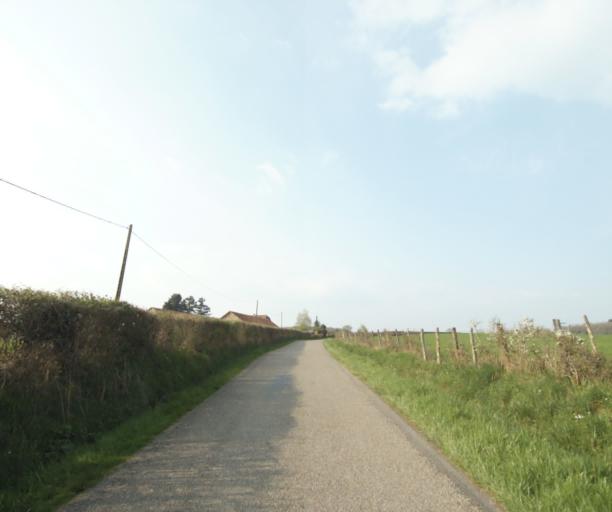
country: FR
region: Bourgogne
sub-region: Departement de Saone-et-Loire
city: Matour
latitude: 46.4707
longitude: 4.4522
